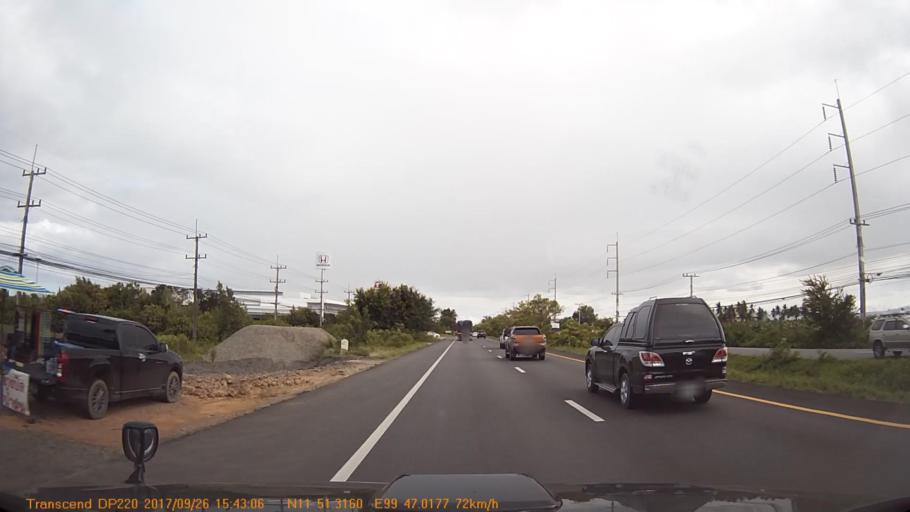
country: TH
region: Prachuap Khiri Khan
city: Prachuap Khiri Khan
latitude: 11.8549
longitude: 99.7836
